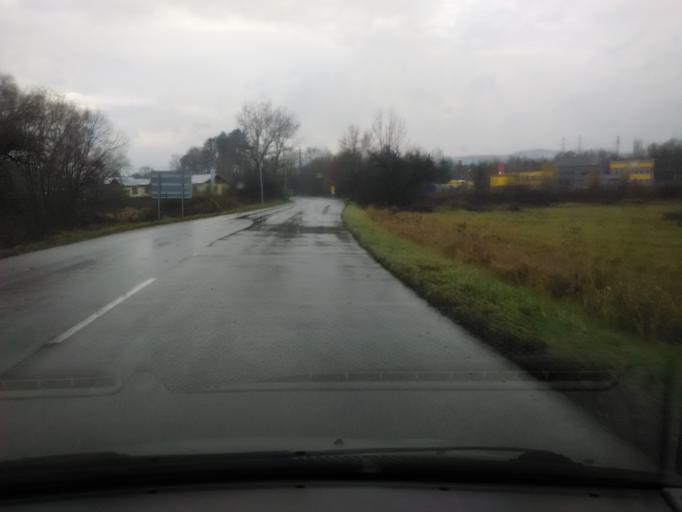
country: SK
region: Zilinsky
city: Bytca
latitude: 49.2164
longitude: 18.5399
